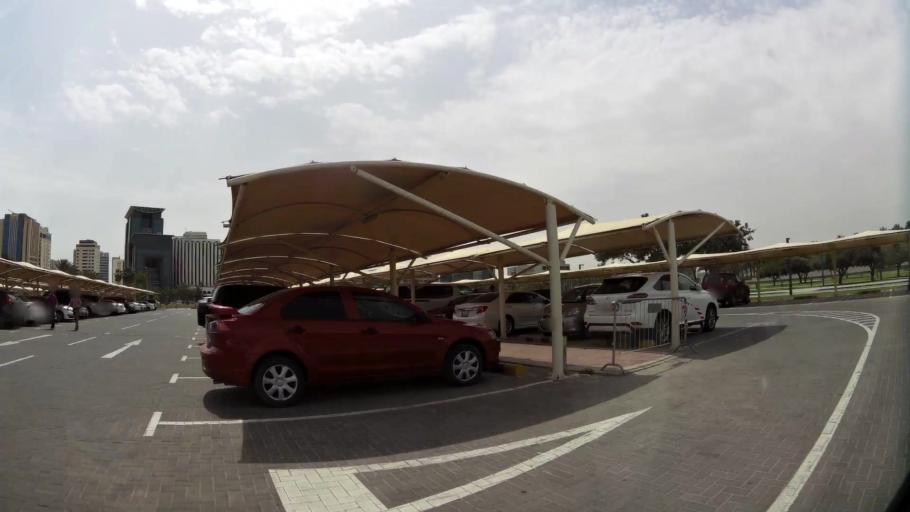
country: QA
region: Baladiyat ad Dawhah
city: Doha
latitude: 25.2934
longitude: 51.5409
